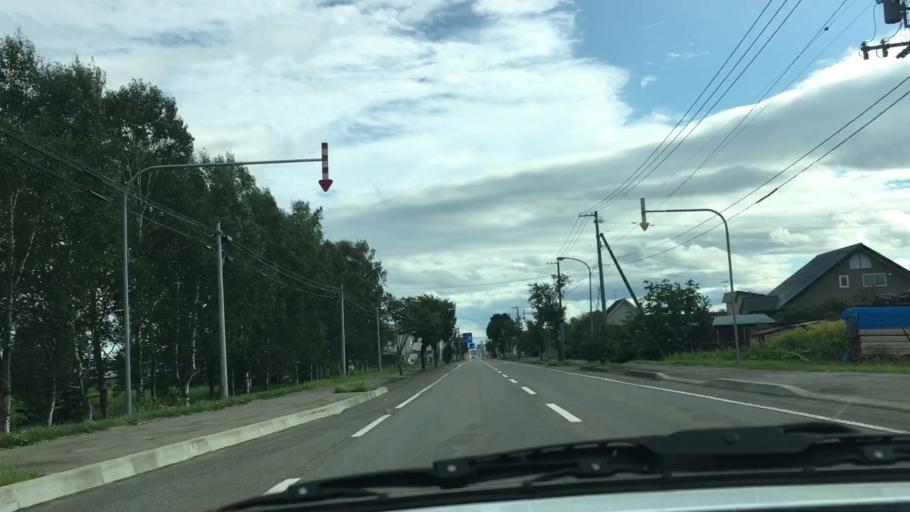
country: JP
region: Hokkaido
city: Otofuke
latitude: 43.2391
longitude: 143.2965
